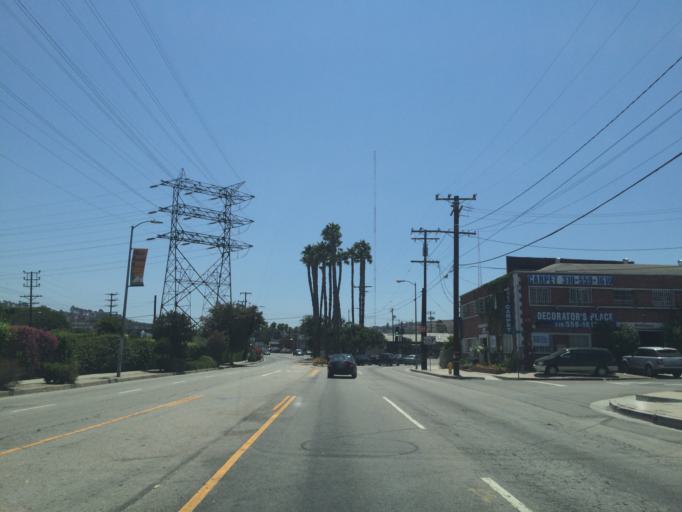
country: US
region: California
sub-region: Los Angeles County
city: Culver City
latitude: 34.0312
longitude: -118.3714
